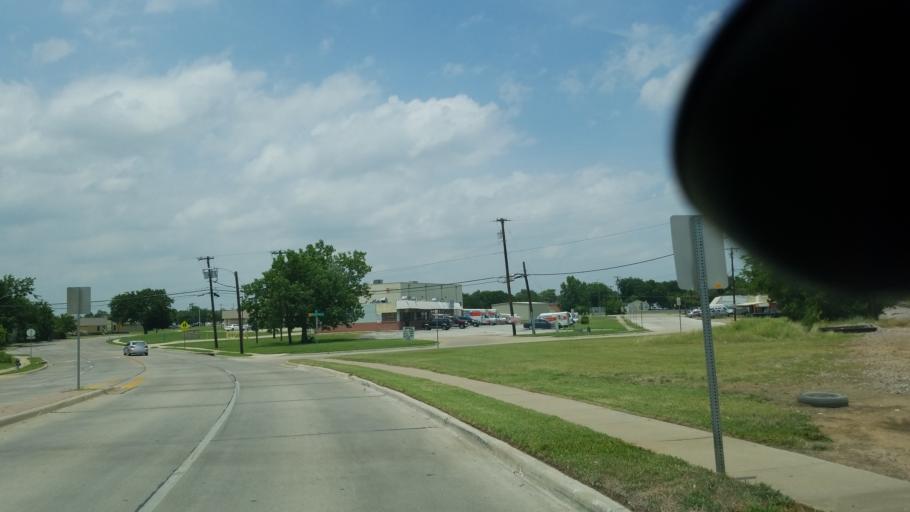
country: US
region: Texas
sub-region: Dallas County
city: Irving
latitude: 32.8271
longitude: -96.9425
